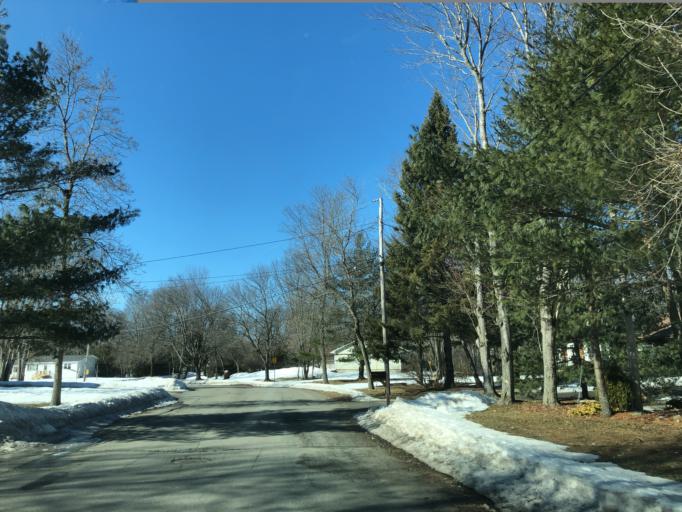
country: US
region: Maine
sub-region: Penobscot County
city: Brewer
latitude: 44.8217
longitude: -68.7495
